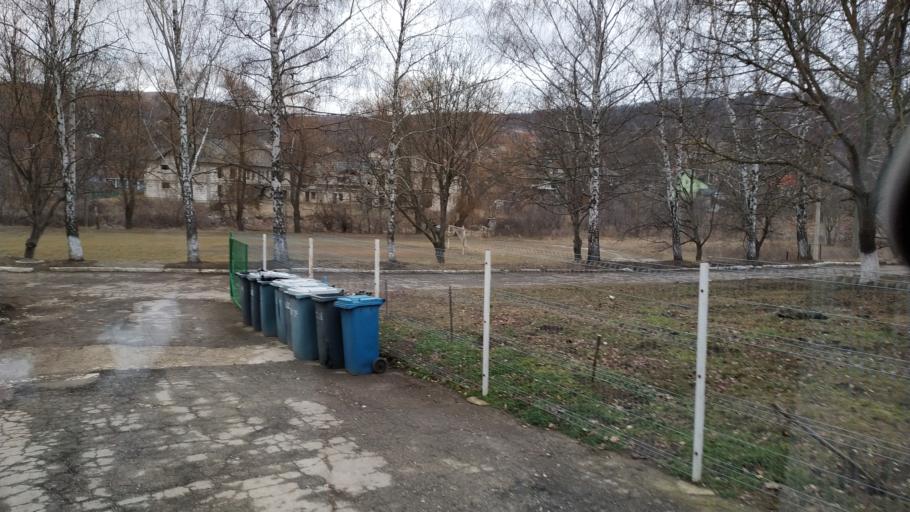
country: MD
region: Calarasi
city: Calarasi
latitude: 47.2387
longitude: 28.3089
